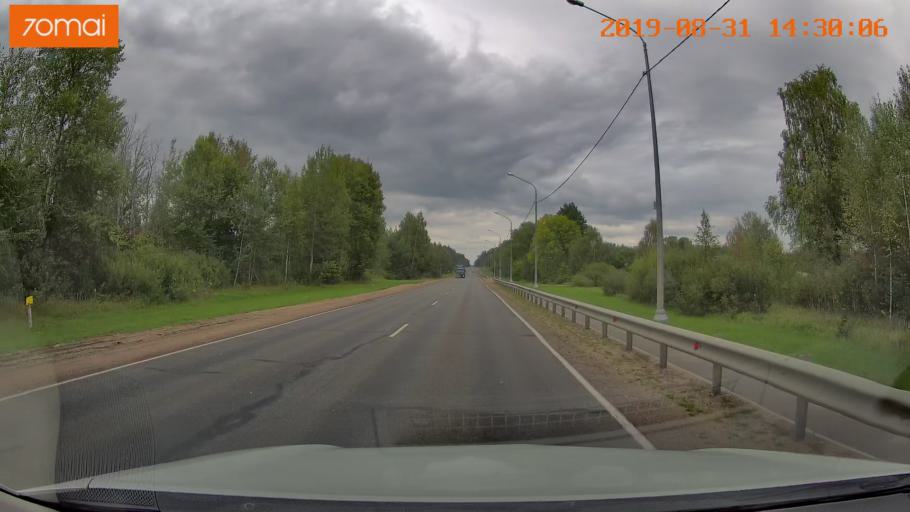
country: RU
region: Smolensk
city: Yekimovichi
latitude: 54.1296
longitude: 33.3445
